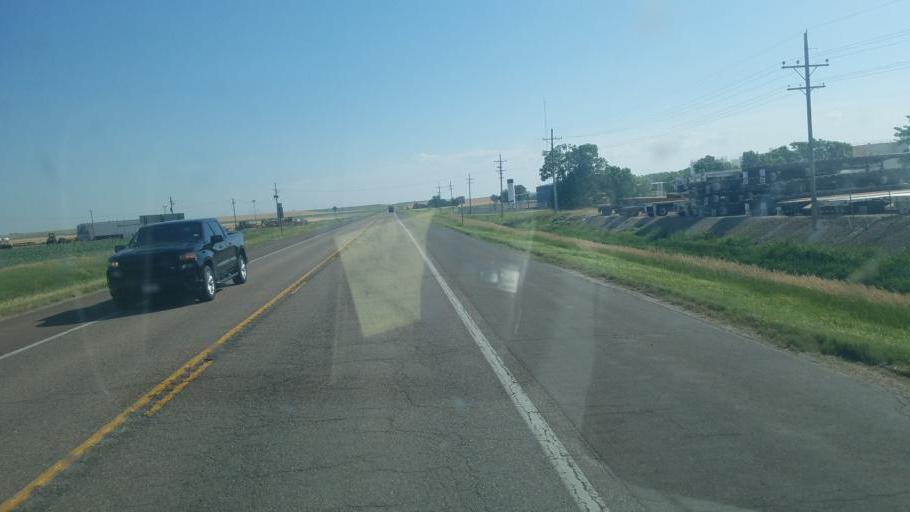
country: US
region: Kansas
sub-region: Barton County
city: Great Bend
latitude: 38.3675
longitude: -98.6940
